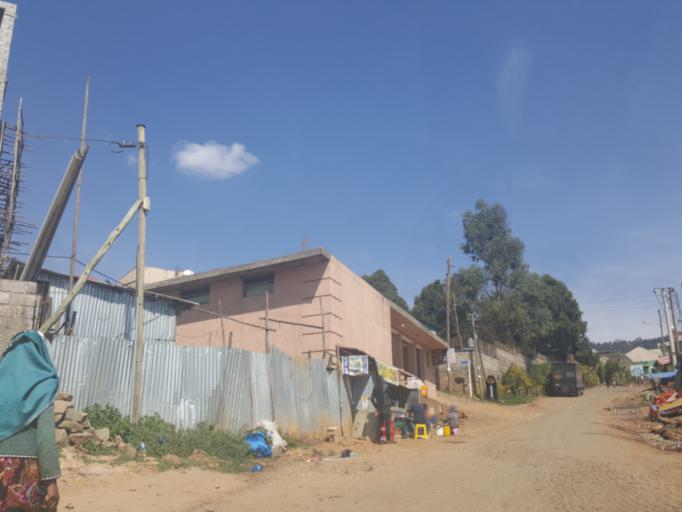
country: ET
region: Adis Abeba
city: Addis Ababa
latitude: 9.0686
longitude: 38.7158
